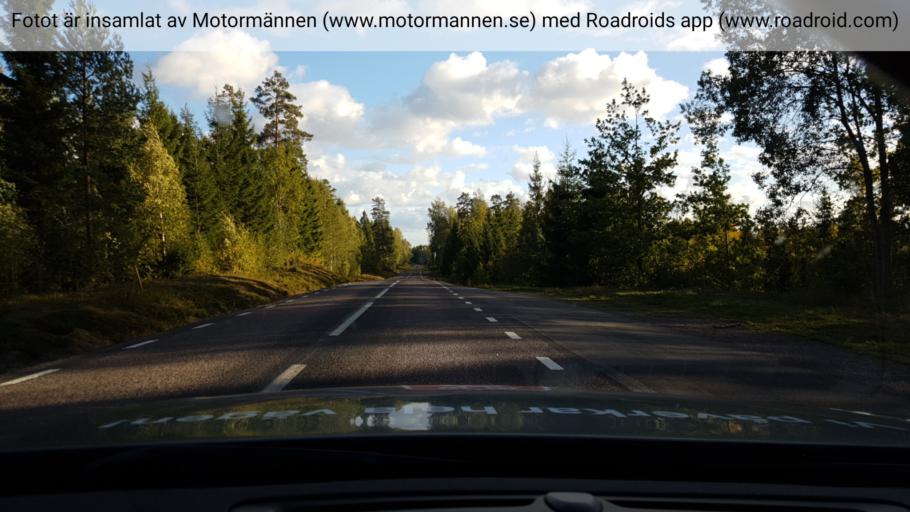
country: SE
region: Vaermland
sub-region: Karlstads Kommun
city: Molkom
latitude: 59.7401
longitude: 13.6783
